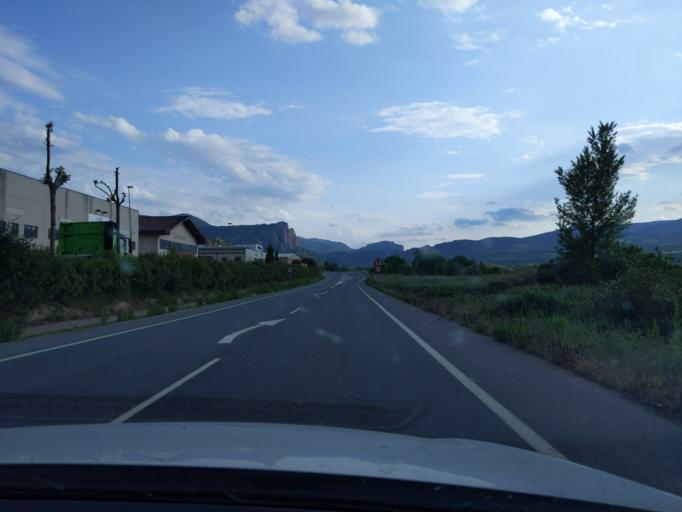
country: ES
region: La Rioja
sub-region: Provincia de La Rioja
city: Albelda de Iregua
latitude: 42.3475
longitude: -2.4791
